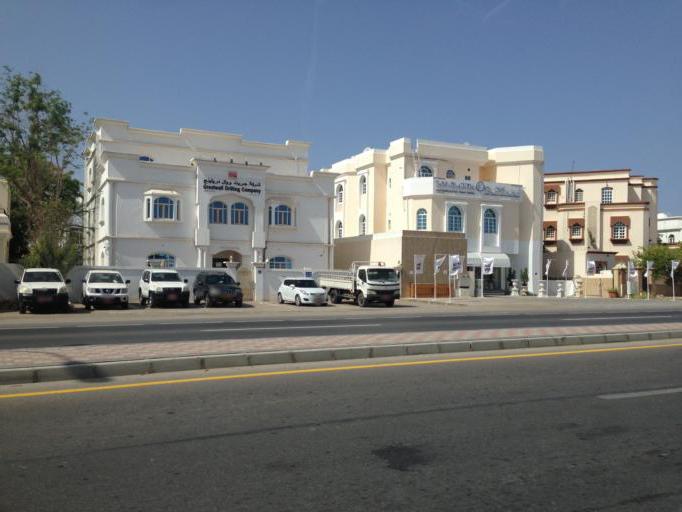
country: OM
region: Muhafazat Masqat
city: Bawshar
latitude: 23.6022
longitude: 58.3640
